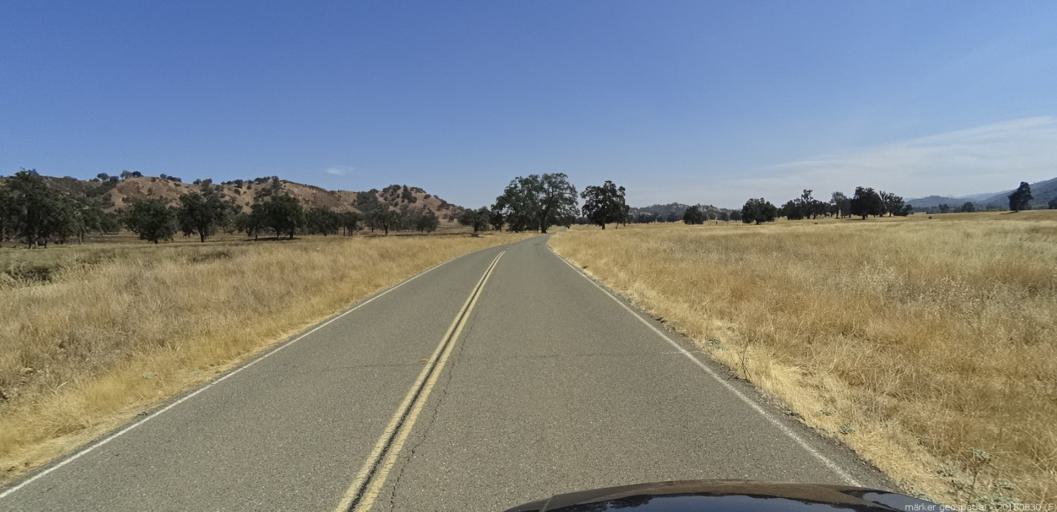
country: US
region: California
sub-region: Monterey County
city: King City
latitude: 35.9695
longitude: -121.3142
